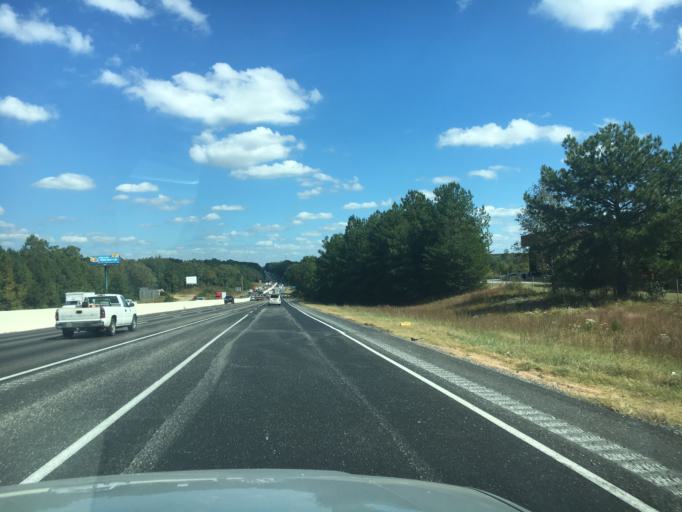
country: US
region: South Carolina
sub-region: Spartanburg County
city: Wellford
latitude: 34.9180
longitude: -82.1007
